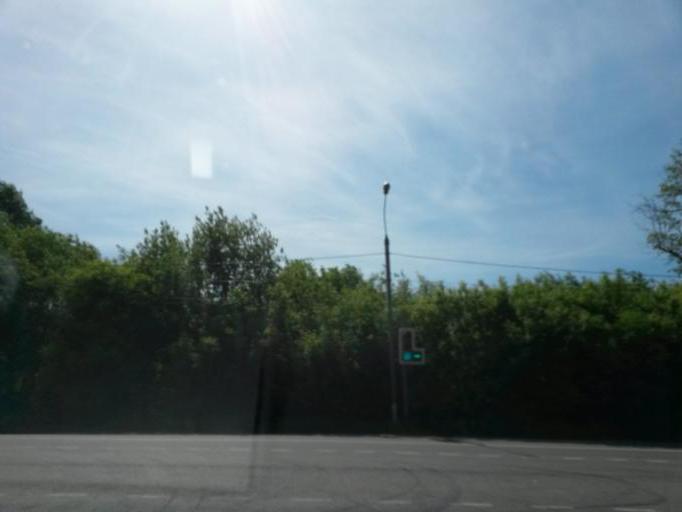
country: RU
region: Moskovskaya
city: Vostryakovo
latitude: 55.4160
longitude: 37.7800
